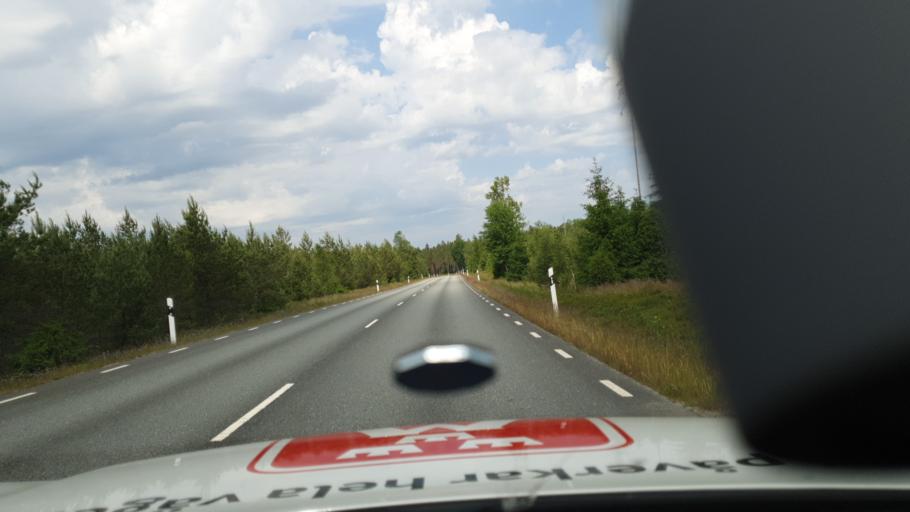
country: SE
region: Joenkoeping
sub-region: Varnamo Kommun
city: Varnamo
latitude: 57.2774
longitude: 14.0603
